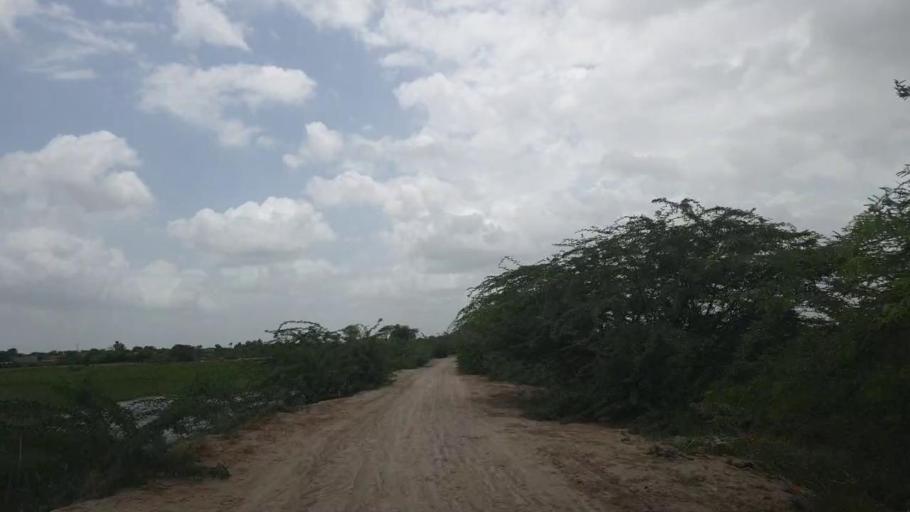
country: PK
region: Sindh
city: Badin
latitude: 24.6514
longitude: 68.9220
